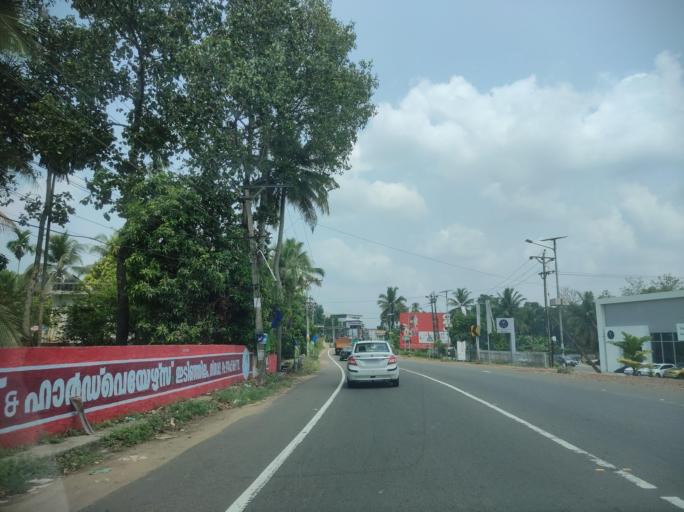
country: IN
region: Kerala
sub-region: Kottayam
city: Changanacheri
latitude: 9.4195
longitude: 76.5477
